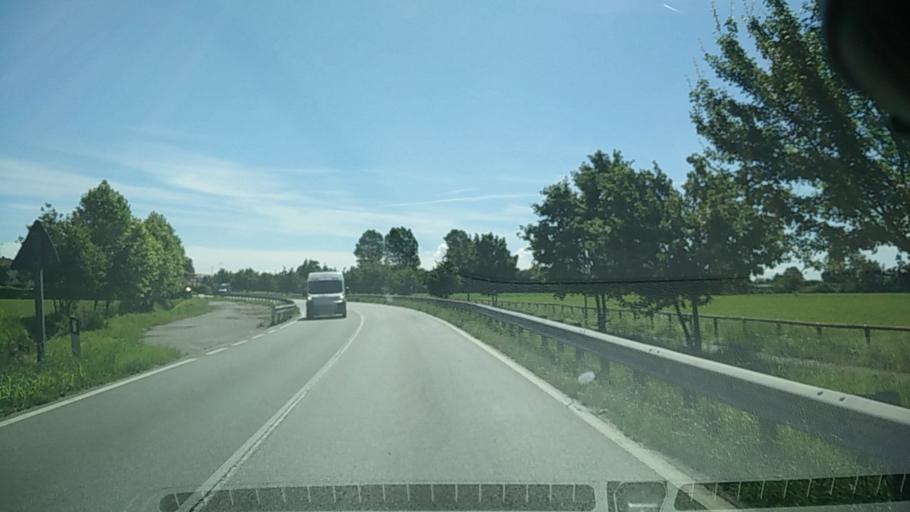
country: IT
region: Veneto
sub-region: Provincia di Venezia
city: Moniego
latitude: 45.5768
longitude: 12.0909
